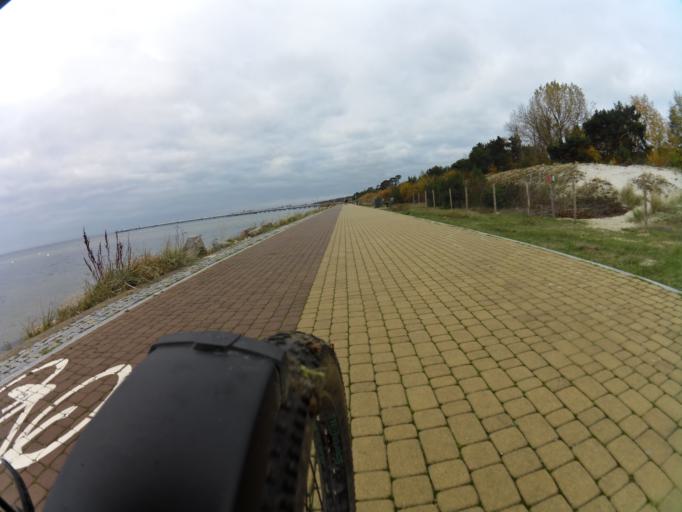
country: PL
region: Pomeranian Voivodeship
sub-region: Powiat pucki
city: Jastarnia
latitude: 54.6793
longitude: 18.7143
